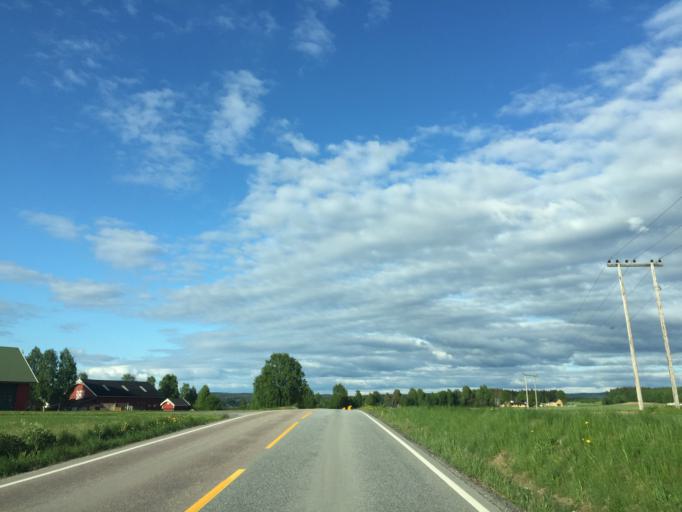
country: NO
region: Akershus
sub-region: Sorum
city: Sorumsand
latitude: 59.9838
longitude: 11.2718
